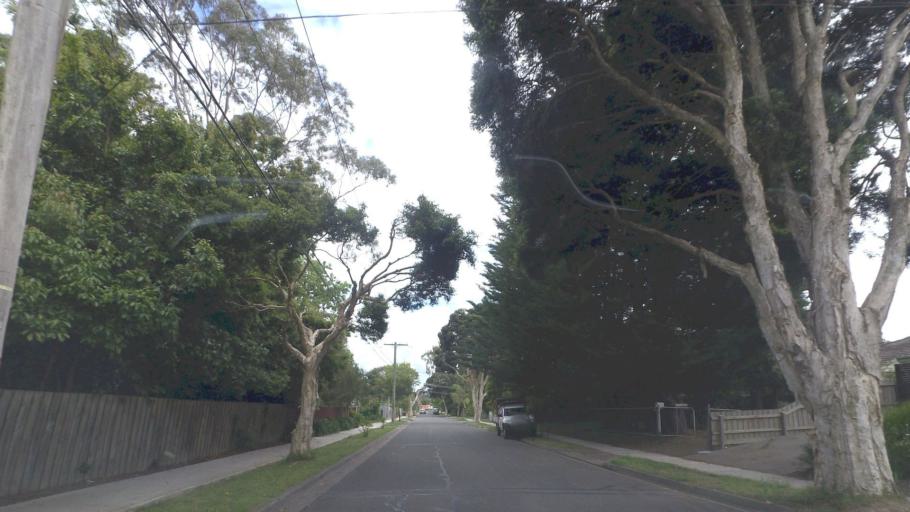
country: AU
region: Victoria
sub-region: Maroondah
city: Croydon Hills
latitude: -37.7923
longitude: 145.2687
